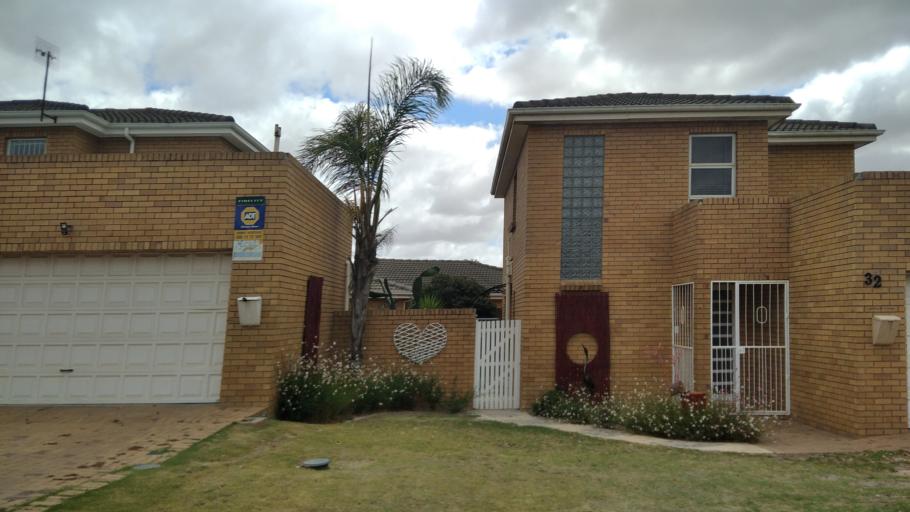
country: ZA
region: Western Cape
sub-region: City of Cape Town
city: Kraaifontein
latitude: -33.8209
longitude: 18.6847
